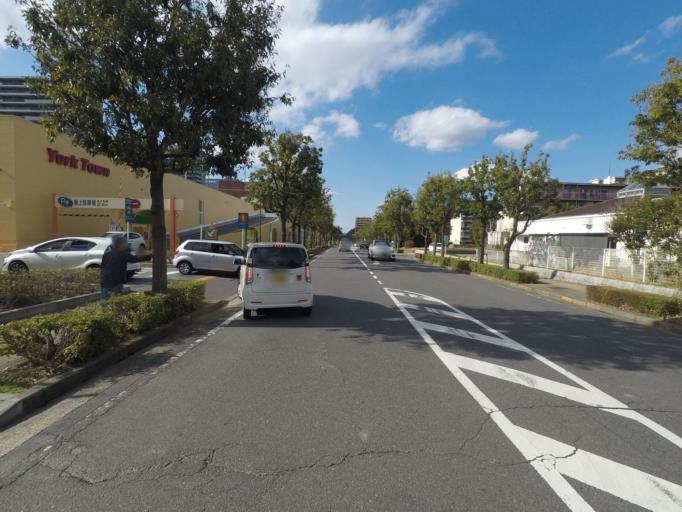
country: JP
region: Ibaraki
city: Naka
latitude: 36.0805
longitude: 140.1181
